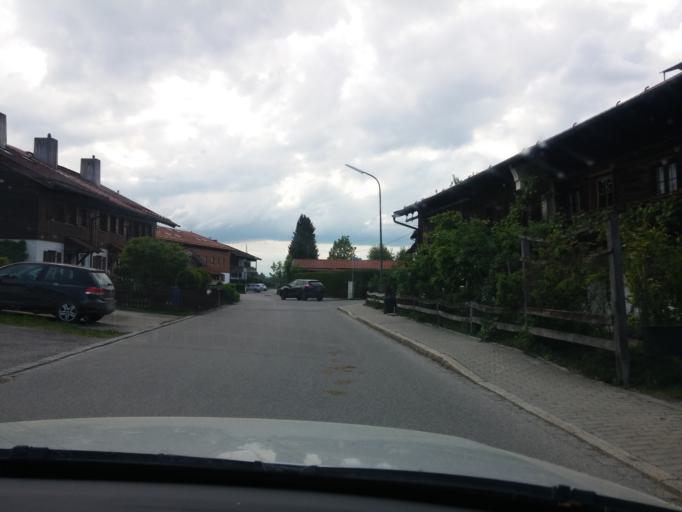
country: DE
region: Bavaria
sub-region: Upper Bavaria
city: Waakirchen
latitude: 47.7730
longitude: 11.6719
